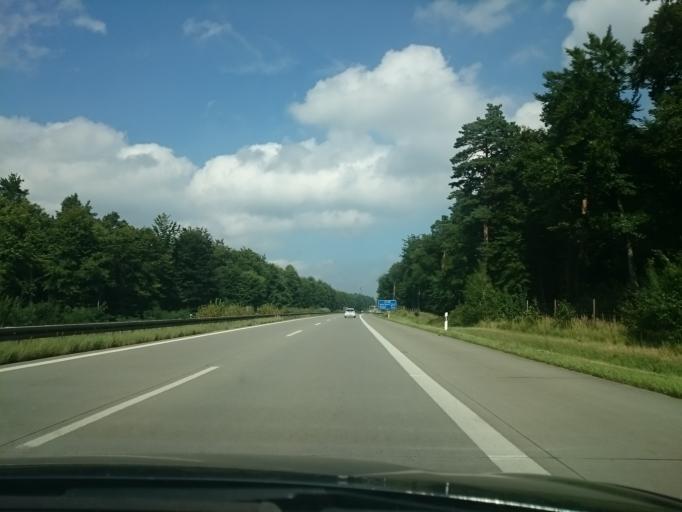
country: DE
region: Brandenburg
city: Bernau bei Berlin
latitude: 52.7319
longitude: 13.5403
